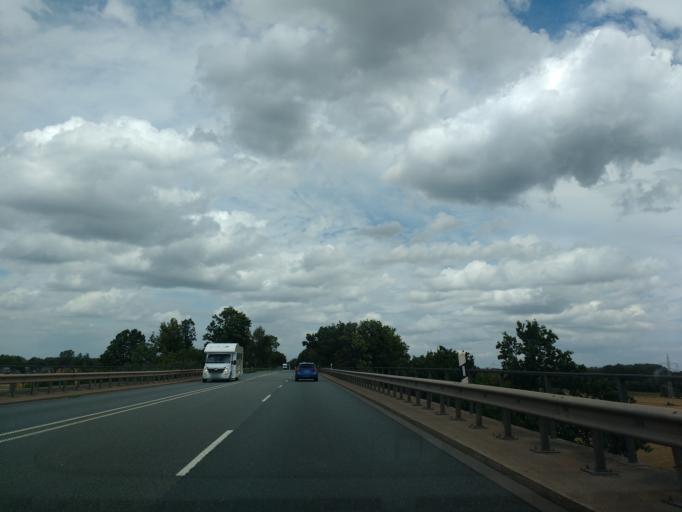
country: DE
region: North Rhine-Westphalia
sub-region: Regierungsbezirk Detmold
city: Minden
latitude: 52.2936
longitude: 8.9772
